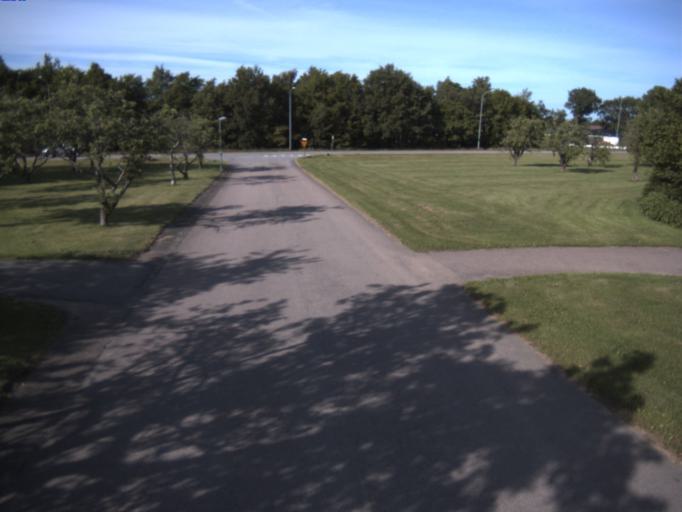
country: SE
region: Skane
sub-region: Helsingborg
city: Odakra
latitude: 56.1014
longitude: 12.7559
